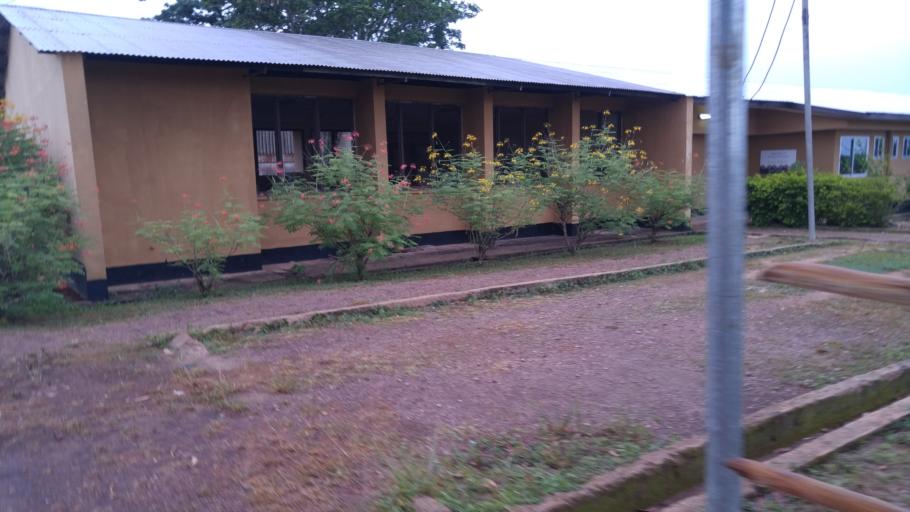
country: SL
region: Southern Province
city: Largo
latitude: 8.1155
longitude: -12.0685
